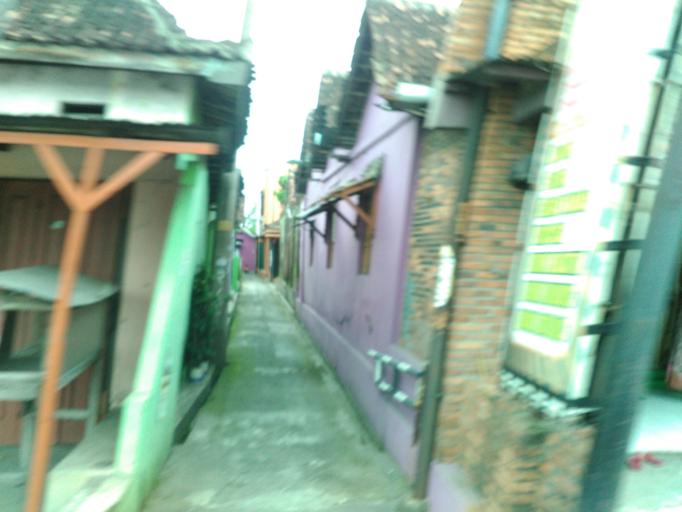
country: ID
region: Central Java
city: Ceper
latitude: -7.6517
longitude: 110.6831
